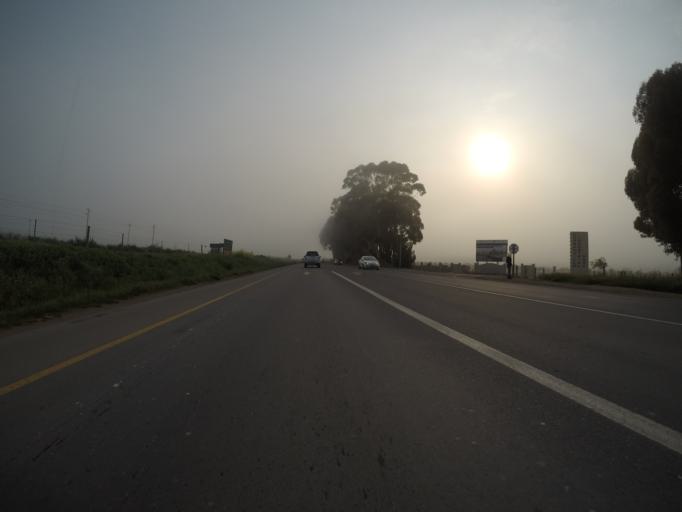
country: ZA
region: Western Cape
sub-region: City of Cape Town
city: Kraaifontein
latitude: -33.7919
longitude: 18.6966
